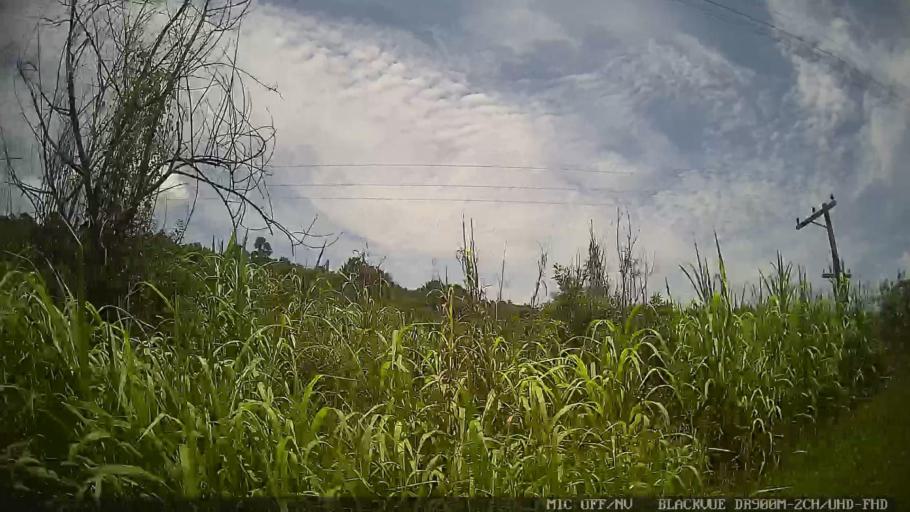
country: BR
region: Sao Paulo
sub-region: Atibaia
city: Atibaia
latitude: -23.0760
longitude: -46.6184
